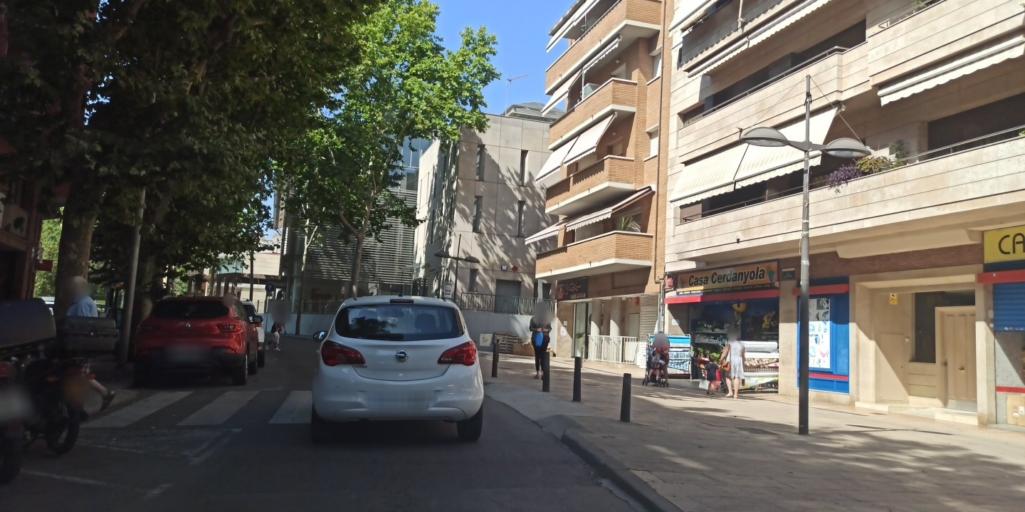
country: ES
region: Catalonia
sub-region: Provincia de Barcelona
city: Cerdanyola del Valles
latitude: 41.4932
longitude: 2.1431
